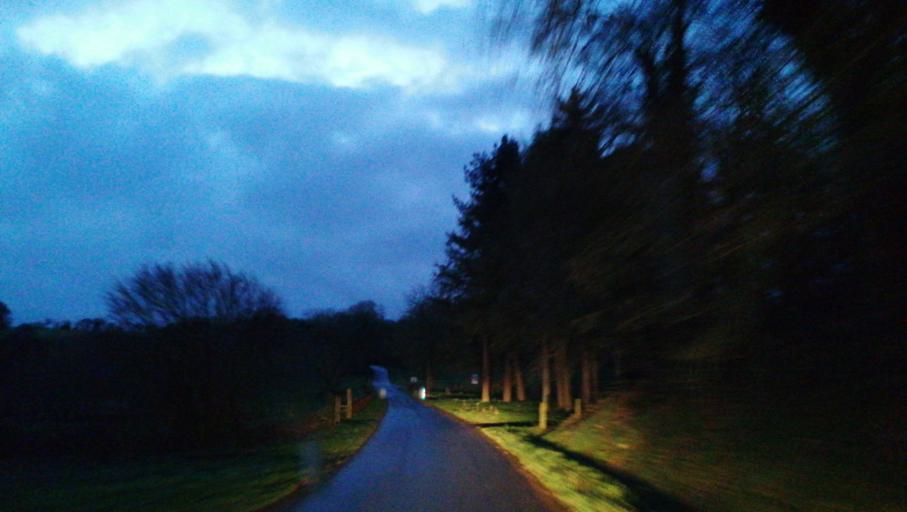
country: FR
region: Brittany
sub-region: Departement des Cotes-d'Armor
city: Plelo
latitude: 48.5594
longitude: -2.9613
